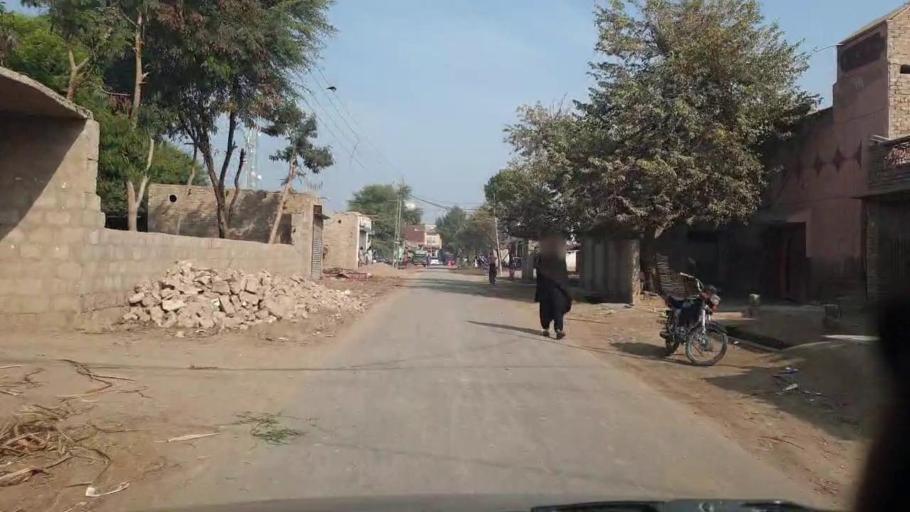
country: PK
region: Sindh
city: Shahdadpur
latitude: 26.0257
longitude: 68.5463
